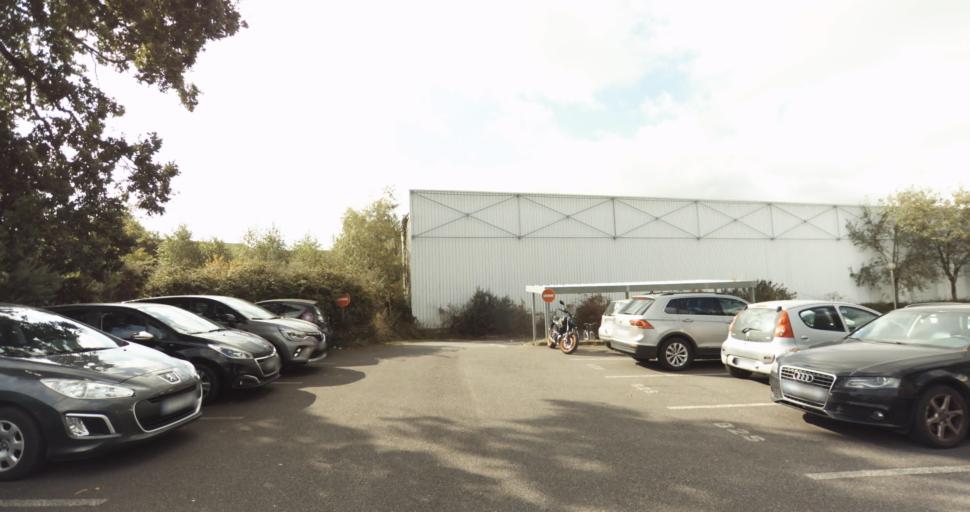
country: FR
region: Brittany
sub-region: Departement d'Ille-et-Vilaine
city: Chantepie
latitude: 48.1024
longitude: -1.6210
